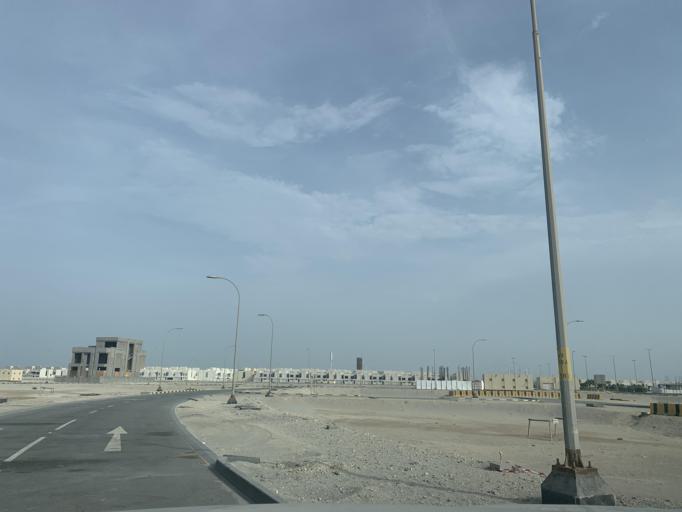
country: BH
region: Muharraq
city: Al Muharraq
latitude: 26.3217
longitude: 50.6246
